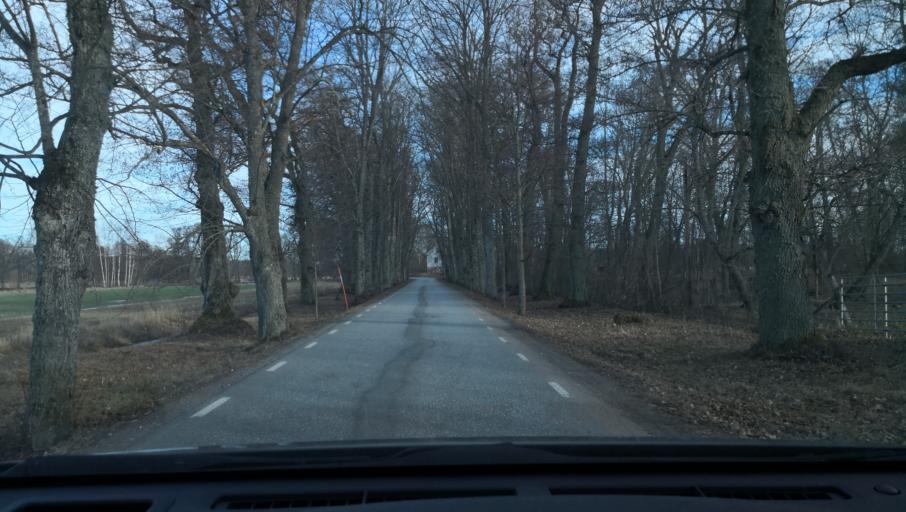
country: SE
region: Uppsala
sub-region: Enkopings Kommun
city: Grillby
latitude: 59.5426
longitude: 17.1974
